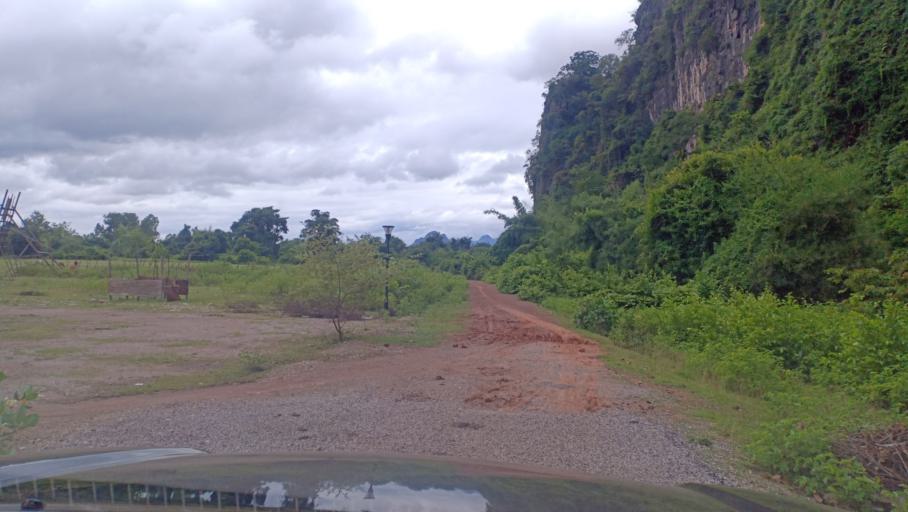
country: LA
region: Khammouan
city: Thakhek
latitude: 17.4303
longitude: 104.8650
